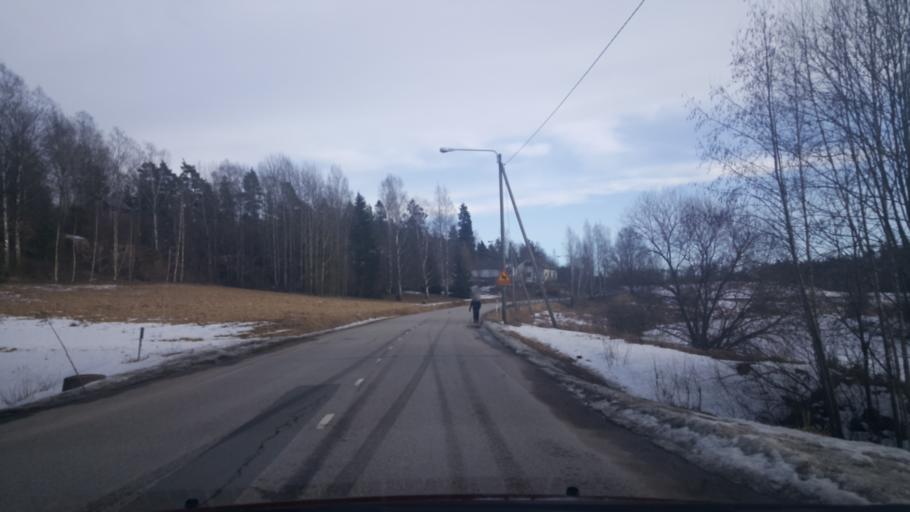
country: FI
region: Uusimaa
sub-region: Helsinki
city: Teekkarikylae
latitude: 60.2922
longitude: 24.8863
